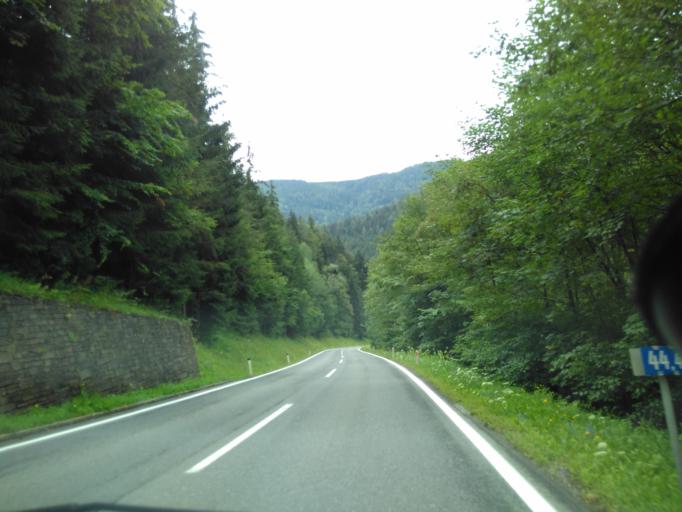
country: AT
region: Styria
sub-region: Politischer Bezirk Graz-Umgebung
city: Schrems bei Frohnleiten
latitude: 47.2767
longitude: 15.3921
